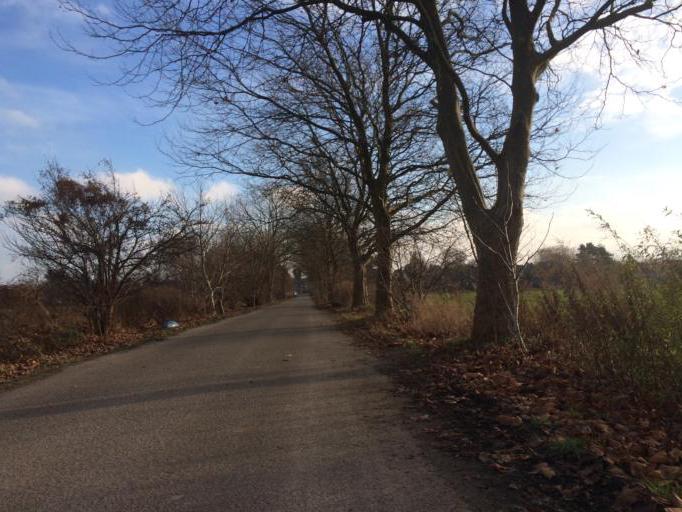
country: DE
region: Berlin
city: Karow
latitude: 52.6043
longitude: 13.4666
